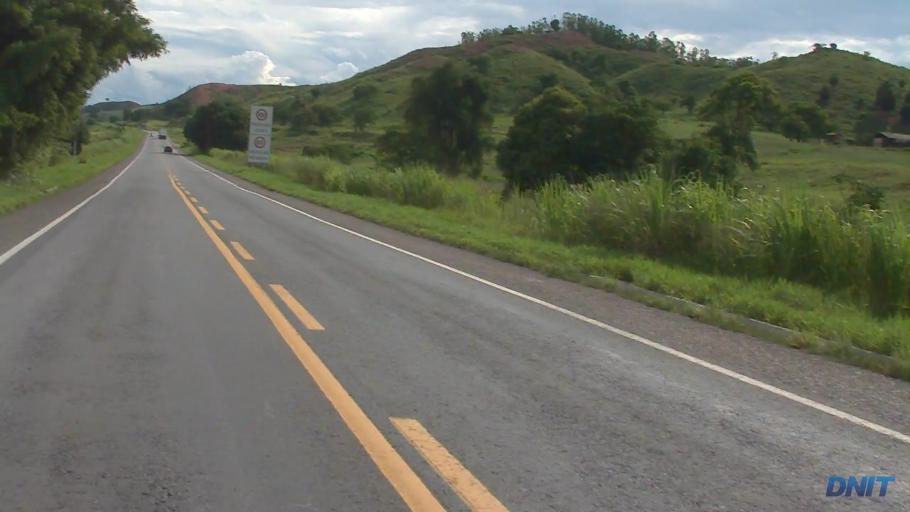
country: BR
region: Minas Gerais
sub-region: Belo Oriente
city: Belo Oriente
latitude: -19.1876
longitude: -42.2680
